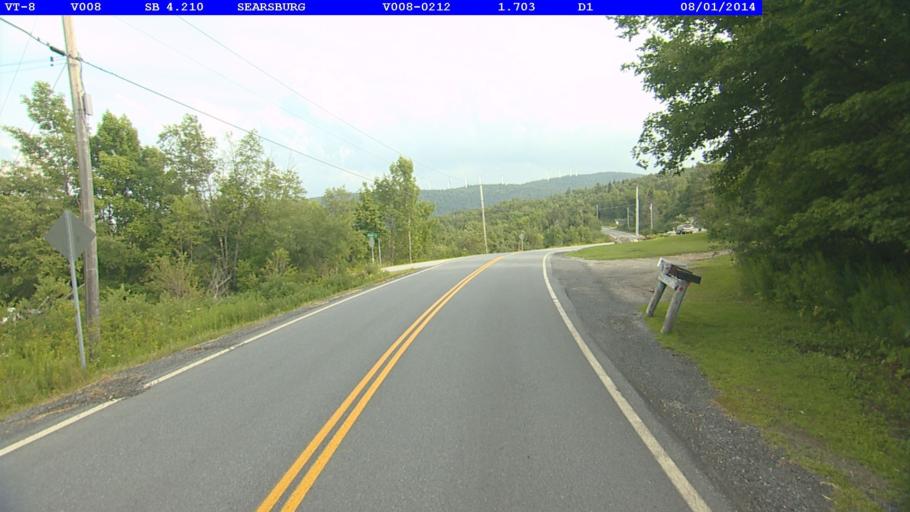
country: US
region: Vermont
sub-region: Windham County
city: Dover
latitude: 42.8815
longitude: -72.9714
